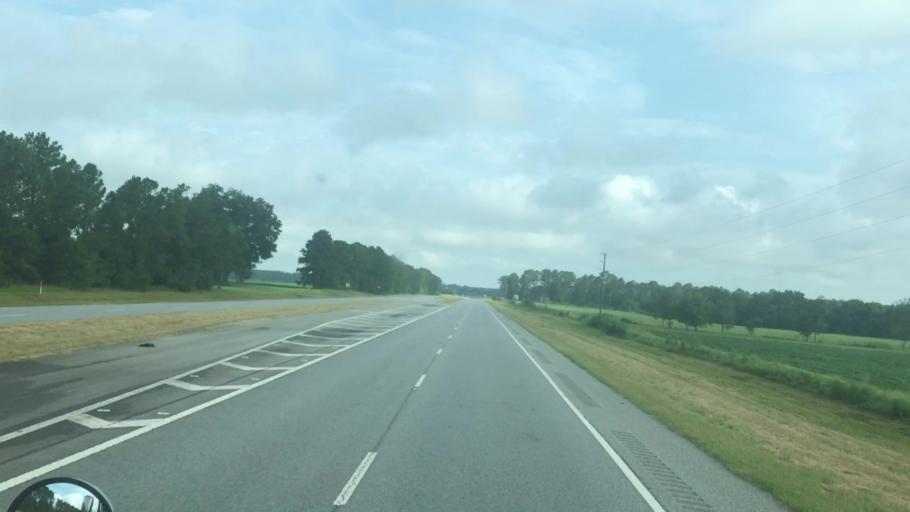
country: US
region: Georgia
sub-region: Miller County
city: Colquitt
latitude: 31.2075
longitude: -84.7726
